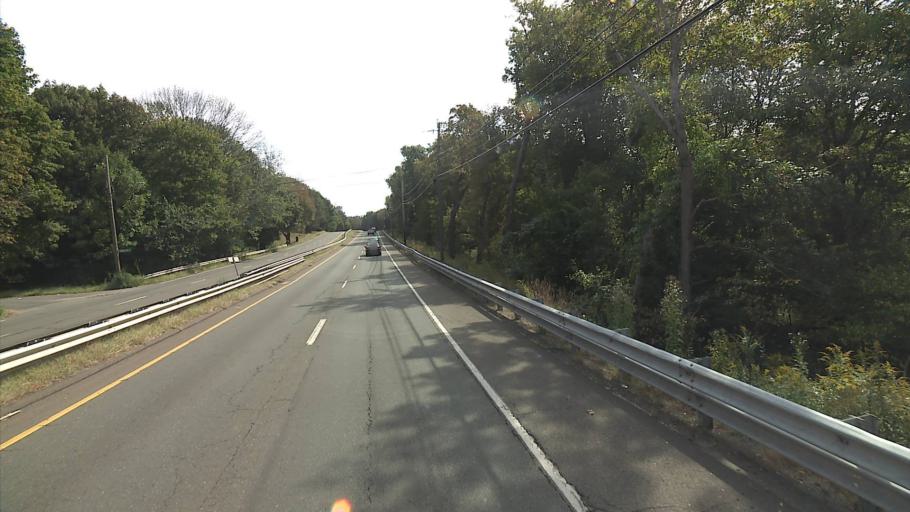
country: US
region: Connecticut
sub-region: New Haven County
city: Orange
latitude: 41.3014
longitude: -73.0250
